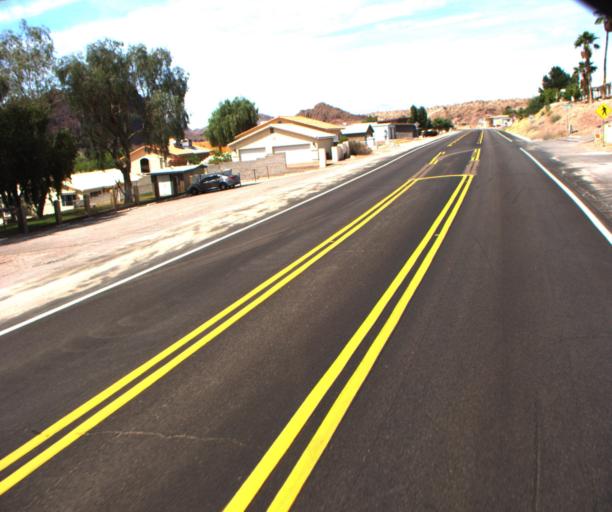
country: US
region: Arizona
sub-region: La Paz County
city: Cienega Springs
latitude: 34.2601
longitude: -114.1294
